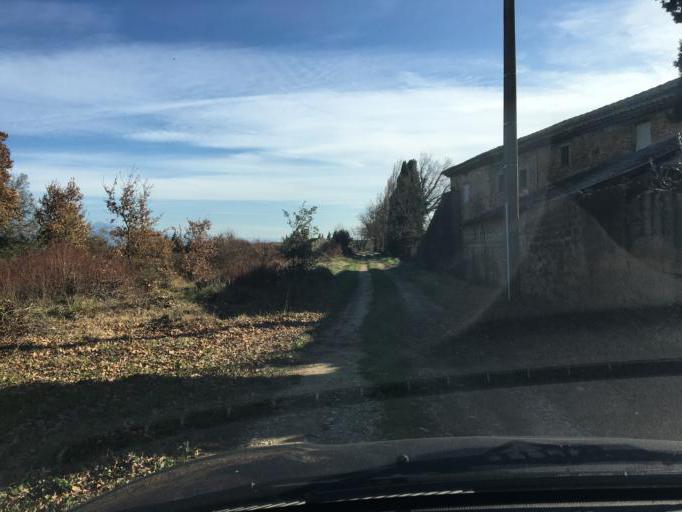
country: FR
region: Provence-Alpes-Cote d'Azur
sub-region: Departement du Vaucluse
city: Camaret-sur-Aigues
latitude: 44.1462
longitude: 4.8950
